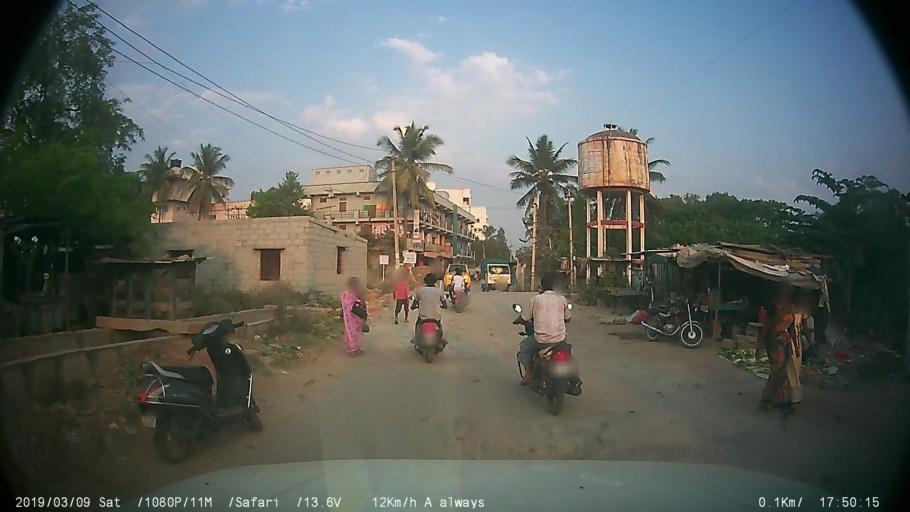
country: IN
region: Karnataka
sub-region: Bangalore Urban
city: Anekal
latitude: 12.8282
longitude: 77.6856
